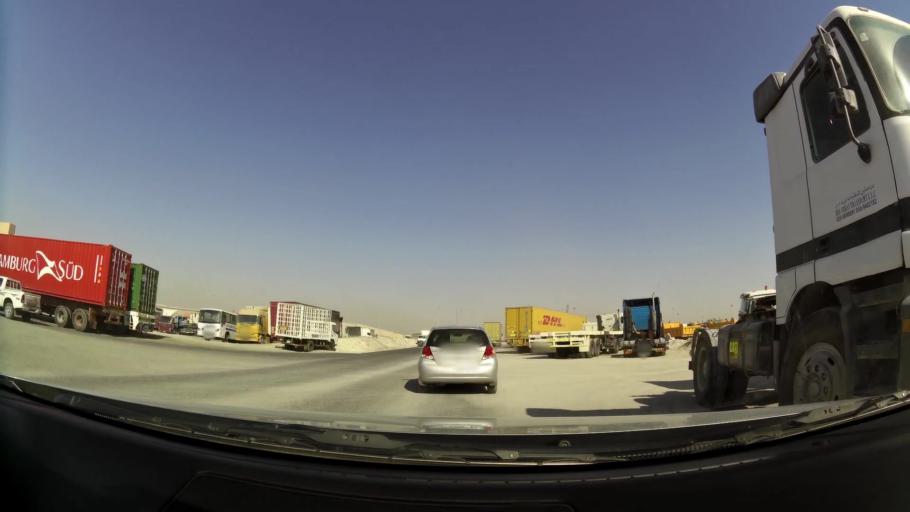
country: AE
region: Dubai
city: Dubai
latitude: 24.9992
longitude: 55.1069
